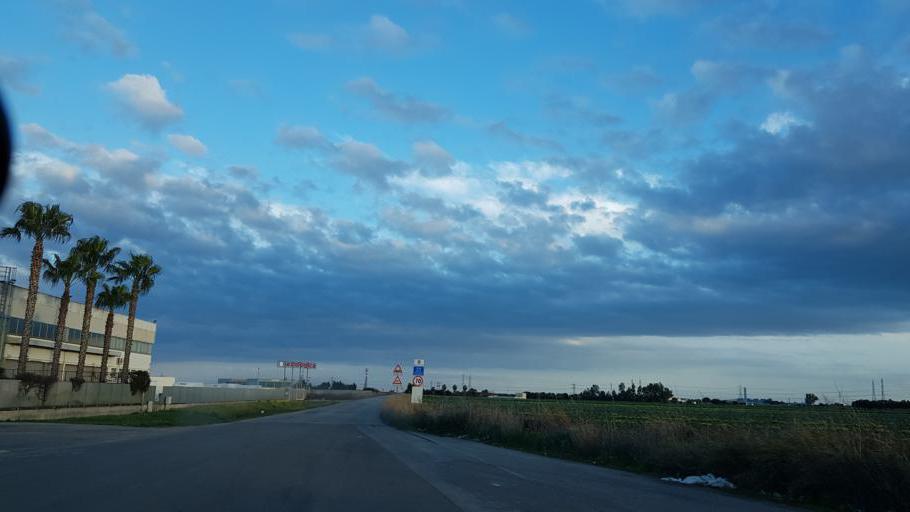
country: IT
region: Apulia
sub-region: Provincia di Brindisi
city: La Rosa
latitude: 40.6189
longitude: 17.9607
